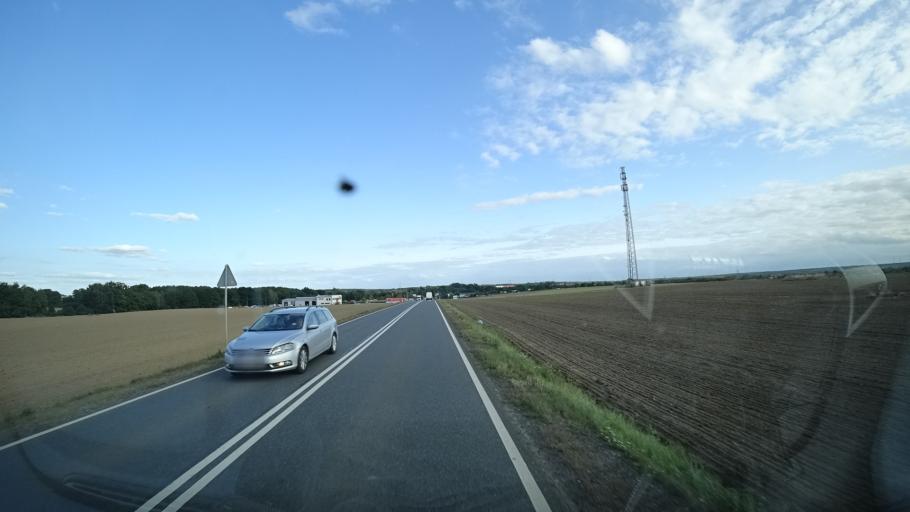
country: PL
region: Silesian Voivodeship
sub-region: Powiat gliwicki
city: Sosnicowice
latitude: 50.2786
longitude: 18.5132
